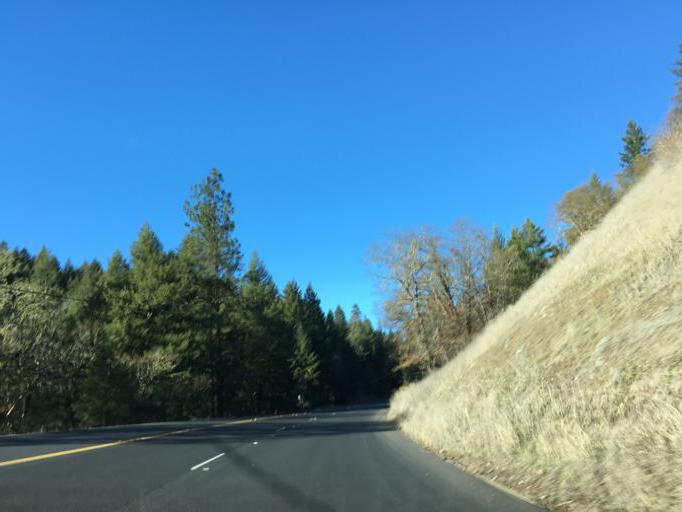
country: US
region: California
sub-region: Mendocino County
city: Laytonville
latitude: 39.7832
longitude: -123.5433
